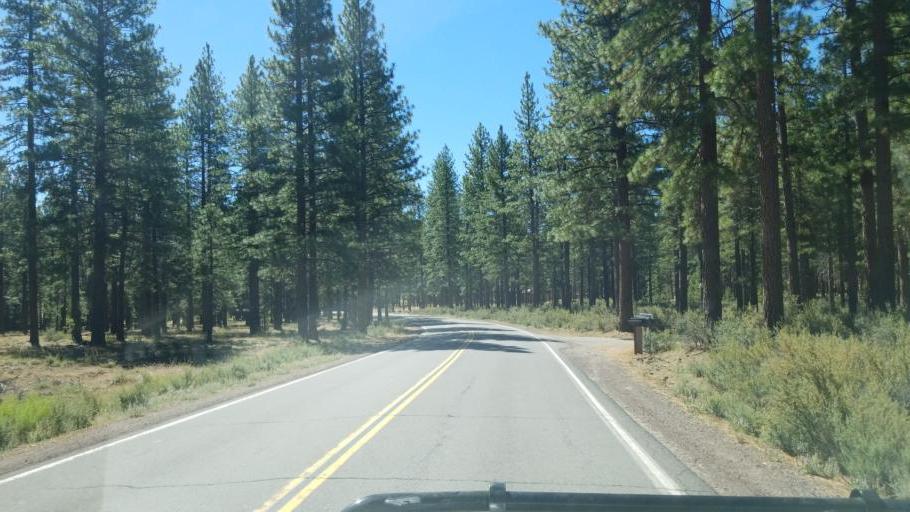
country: US
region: California
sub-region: Lassen County
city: Susanville
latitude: 40.4246
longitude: -120.7228
